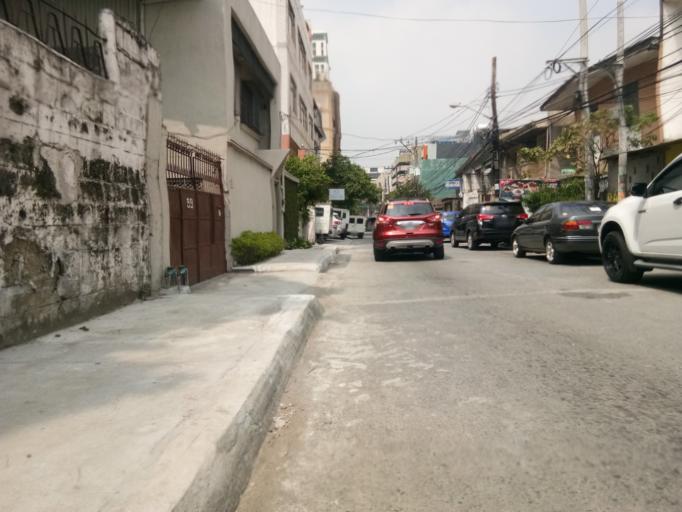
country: PH
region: Metro Manila
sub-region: San Juan
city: San Juan
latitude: 14.6164
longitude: 121.0564
